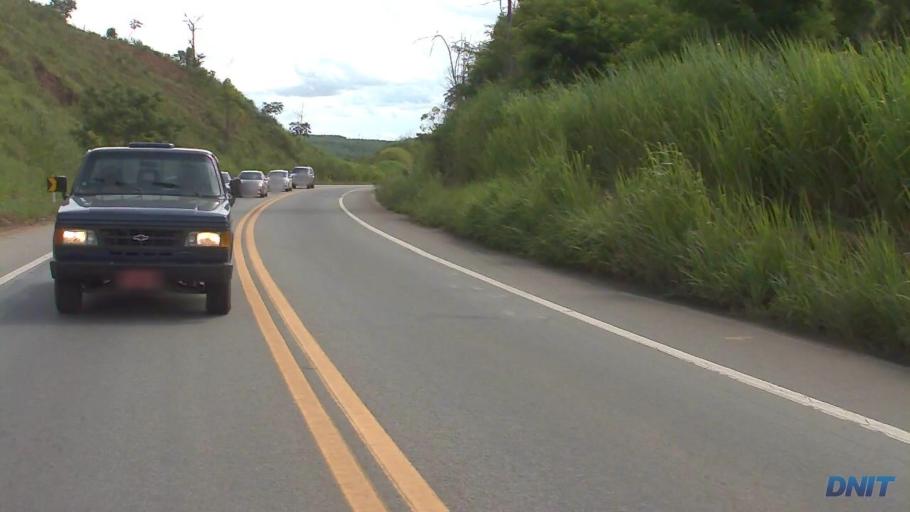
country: BR
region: Minas Gerais
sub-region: Ipaba
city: Ipaba
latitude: -19.3832
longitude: -42.4694
